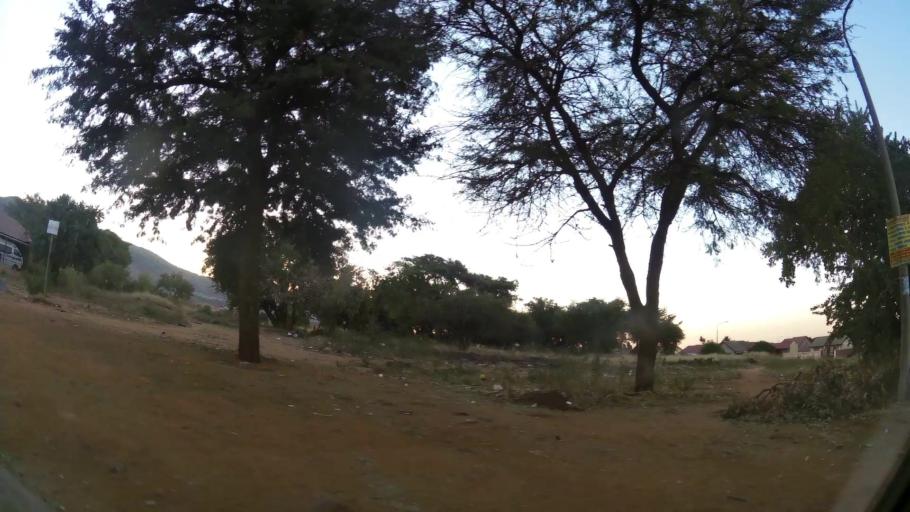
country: ZA
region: North-West
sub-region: Bojanala Platinum District Municipality
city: Rustenburg
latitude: -25.6492
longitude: 27.2098
